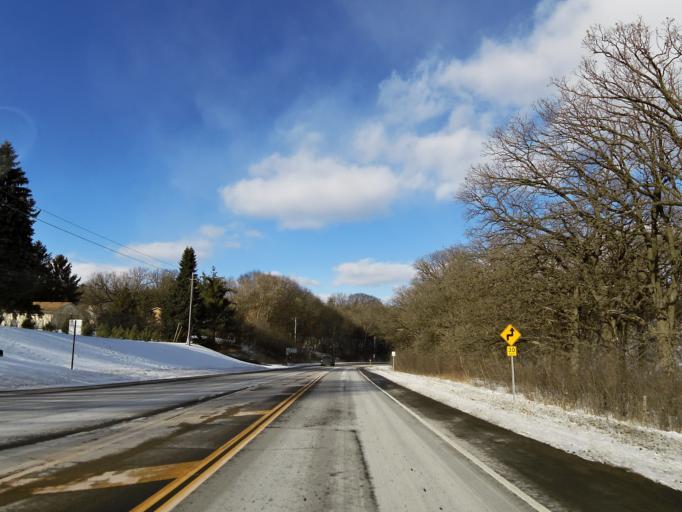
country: US
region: Minnesota
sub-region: Washington County
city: Oak Park Heights
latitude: 45.0183
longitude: -92.7974
